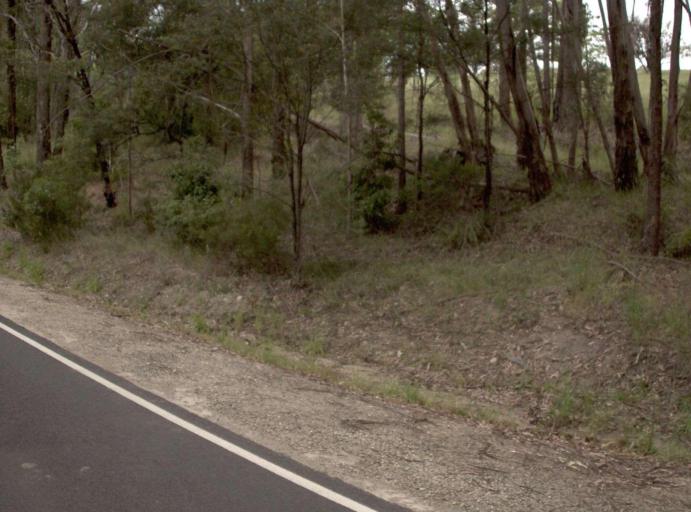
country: AU
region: New South Wales
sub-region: Bombala
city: Bombala
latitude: -37.4577
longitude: 149.1889
